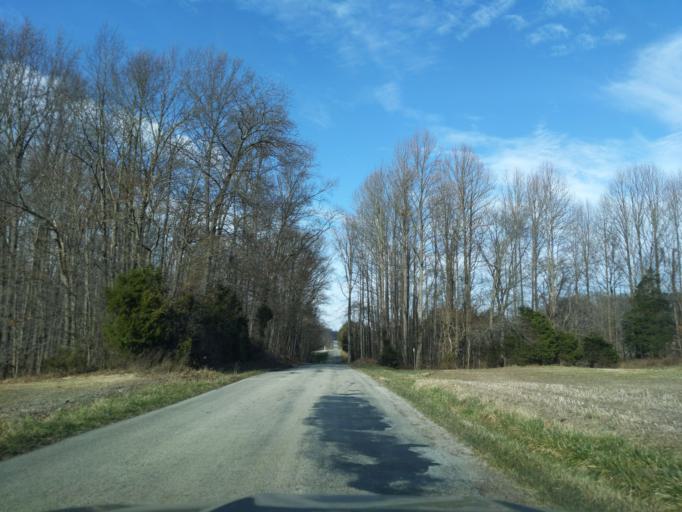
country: US
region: Indiana
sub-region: Decatur County
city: Greensburg
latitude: 39.2802
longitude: -85.4236
